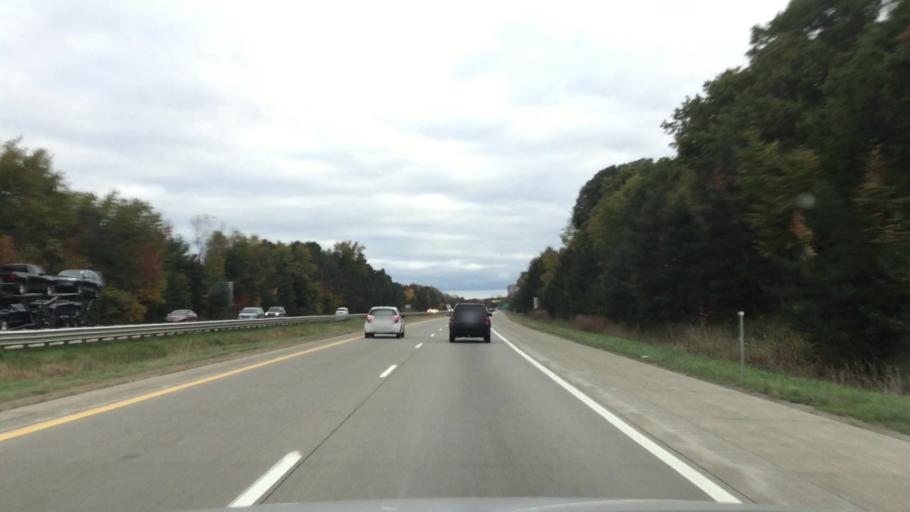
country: US
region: Michigan
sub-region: Genesee County
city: Lake Fenton
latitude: 42.9220
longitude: -83.7258
